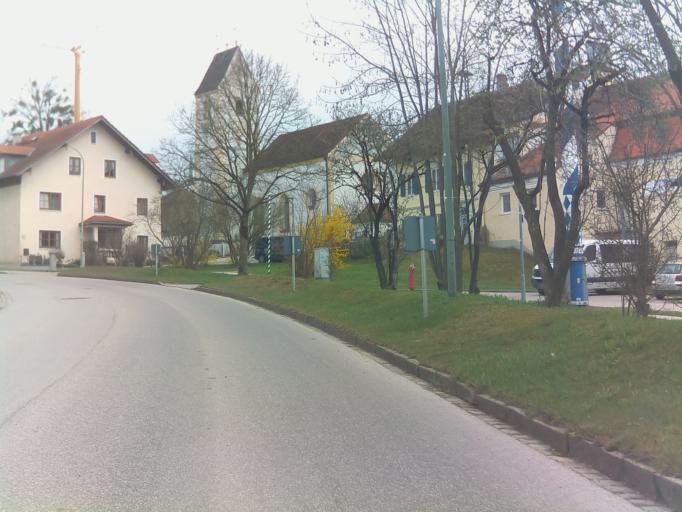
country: DE
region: Bavaria
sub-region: Upper Bavaria
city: Weilheim
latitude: 47.8219
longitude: 11.1906
